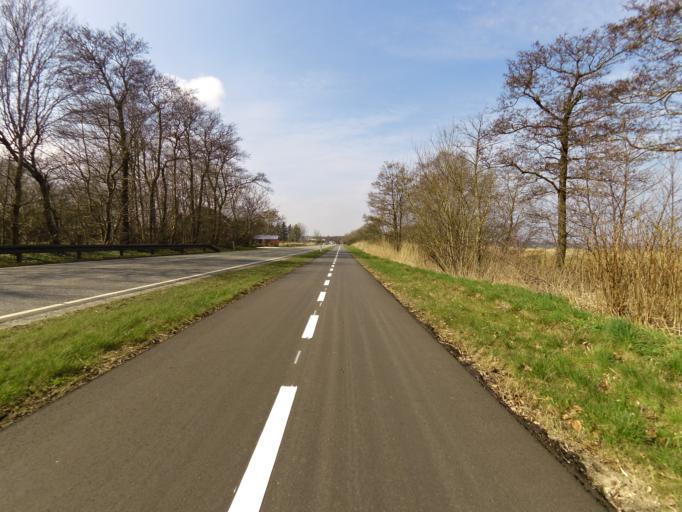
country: DK
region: Central Jutland
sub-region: Struer Kommune
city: Struer
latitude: 56.4711
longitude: 8.6291
